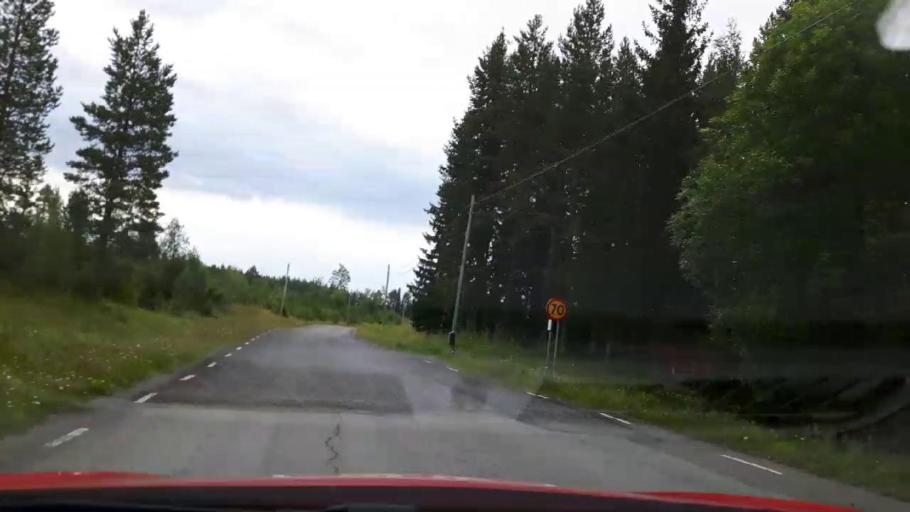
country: SE
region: Jaemtland
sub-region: OEstersunds Kommun
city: Lit
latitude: 63.3938
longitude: 15.0093
